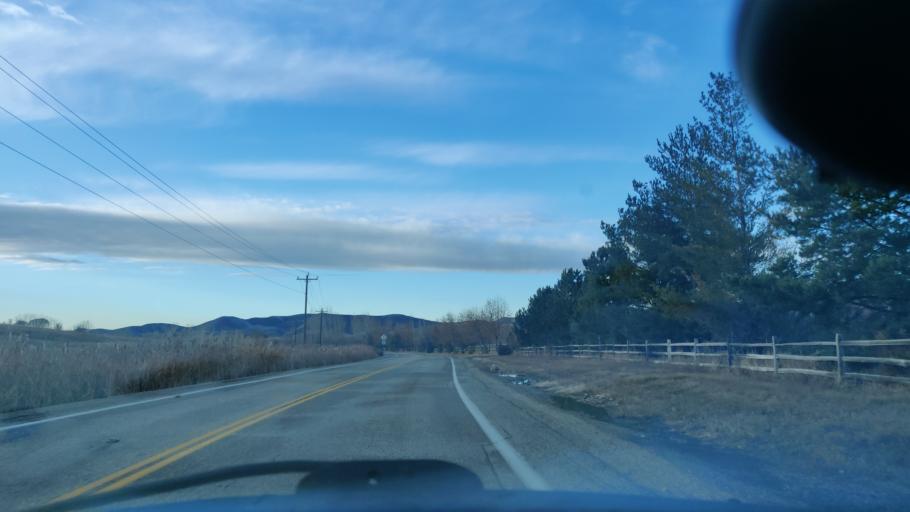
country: US
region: Idaho
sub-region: Ada County
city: Eagle
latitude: 43.7281
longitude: -116.2611
